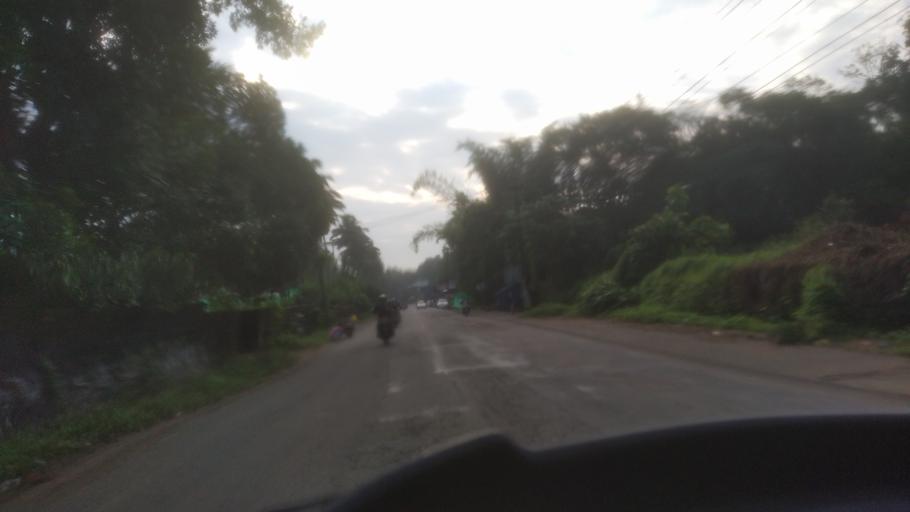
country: IN
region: Kerala
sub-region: Ernakulam
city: Kotamangalam
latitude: 10.0940
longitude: 76.5588
